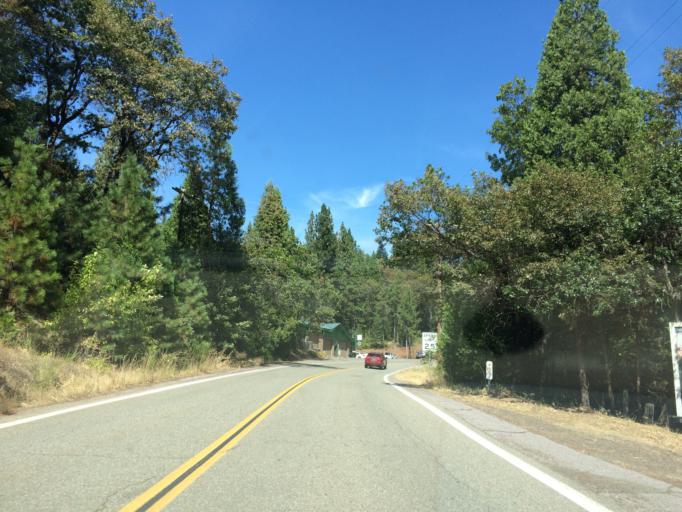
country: US
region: California
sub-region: Siskiyou County
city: Dunsmuir
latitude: 41.1969
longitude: -122.2802
